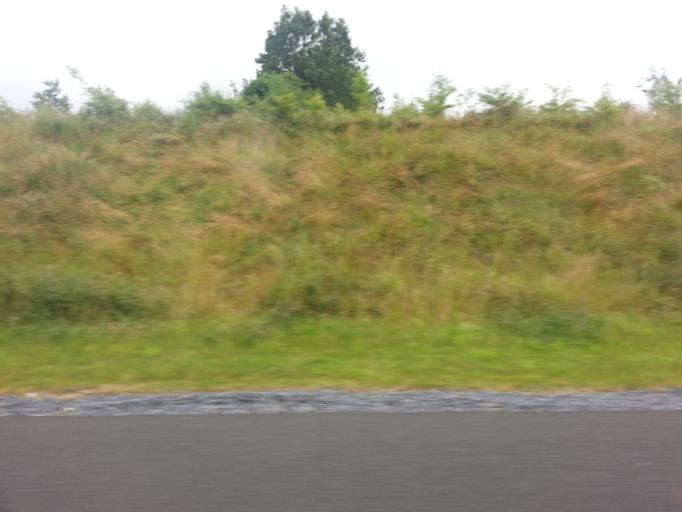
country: IE
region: Leinster
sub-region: Kilkenny
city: Kilkenny
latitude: 52.6560
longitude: -7.2021
